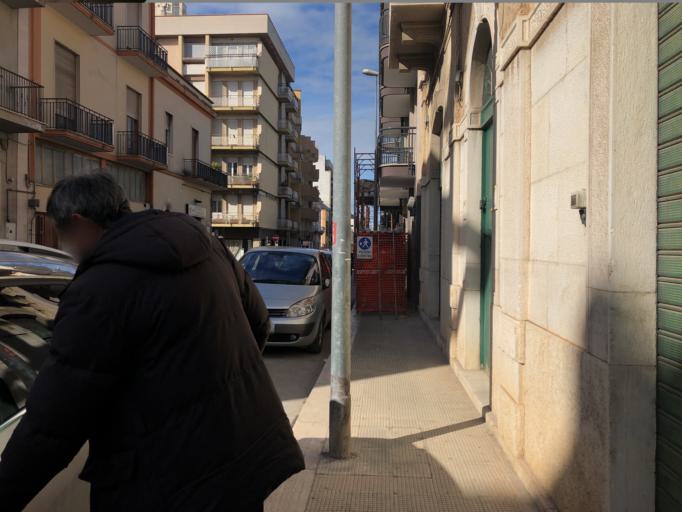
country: IT
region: Apulia
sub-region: Provincia di Barletta - Andria - Trani
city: Andria
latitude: 41.2211
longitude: 16.3032
